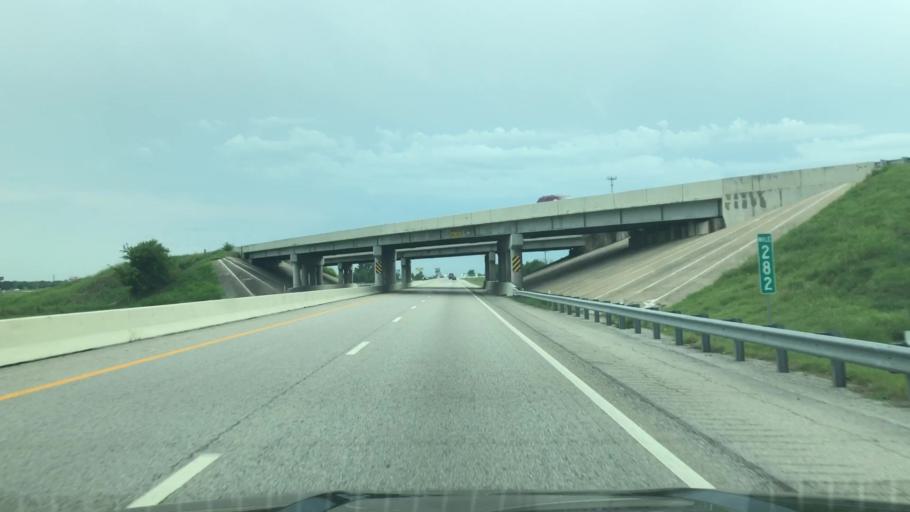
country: US
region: Oklahoma
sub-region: Craig County
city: Vinita
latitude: 36.5589
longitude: -95.2196
